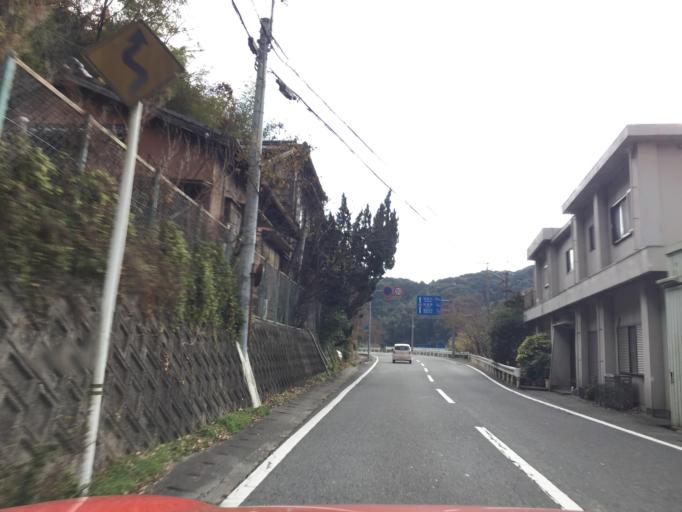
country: JP
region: Wakayama
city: Kainan
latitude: 34.1650
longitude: 135.2523
